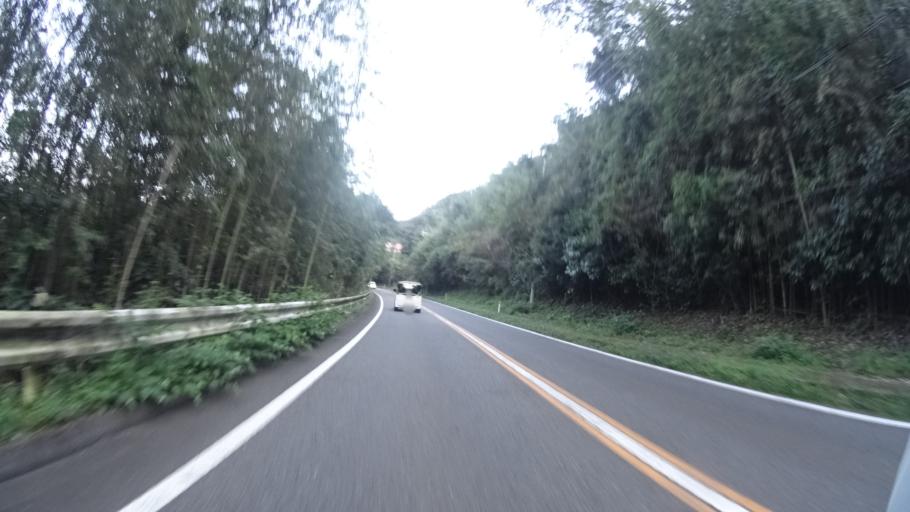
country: JP
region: Oita
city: Hiji
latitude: 33.3482
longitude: 131.4518
